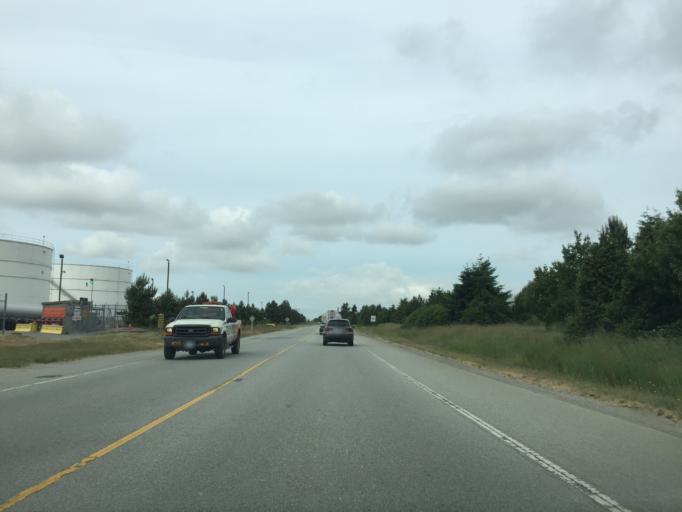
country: CA
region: British Columbia
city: Richmond
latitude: 49.2050
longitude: -123.1561
